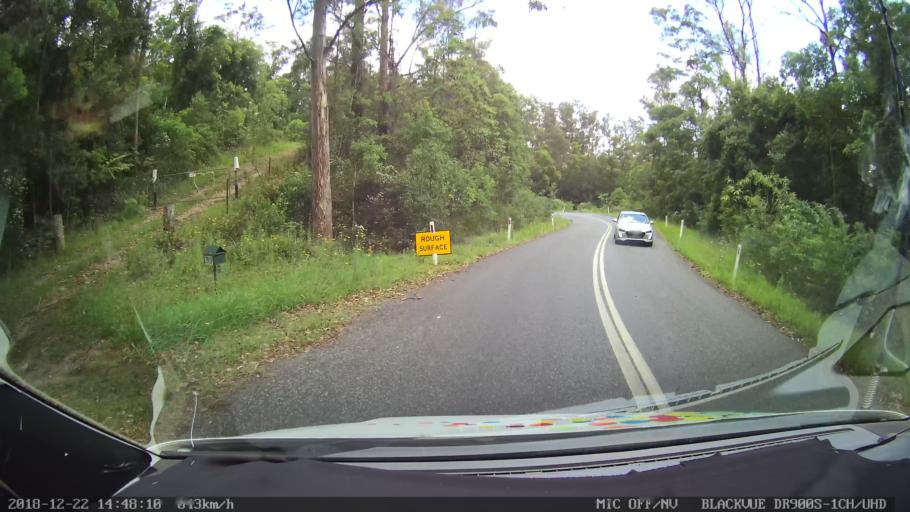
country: AU
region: New South Wales
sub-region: Bellingen
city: Dorrigo
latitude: -30.1798
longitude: 152.5537
